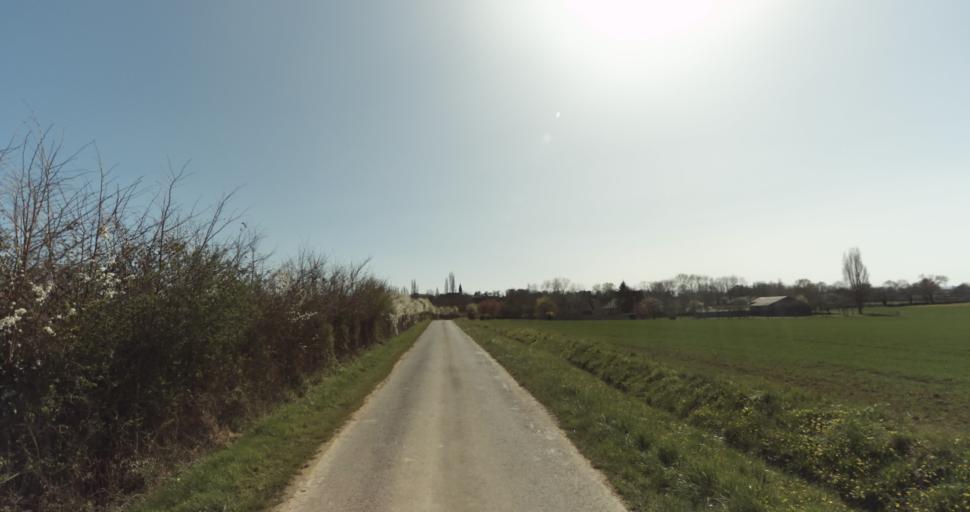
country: FR
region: Lower Normandy
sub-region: Departement du Calvados
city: Saint-Pierre-sur-Dives
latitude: 48.9491
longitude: -0.0044
